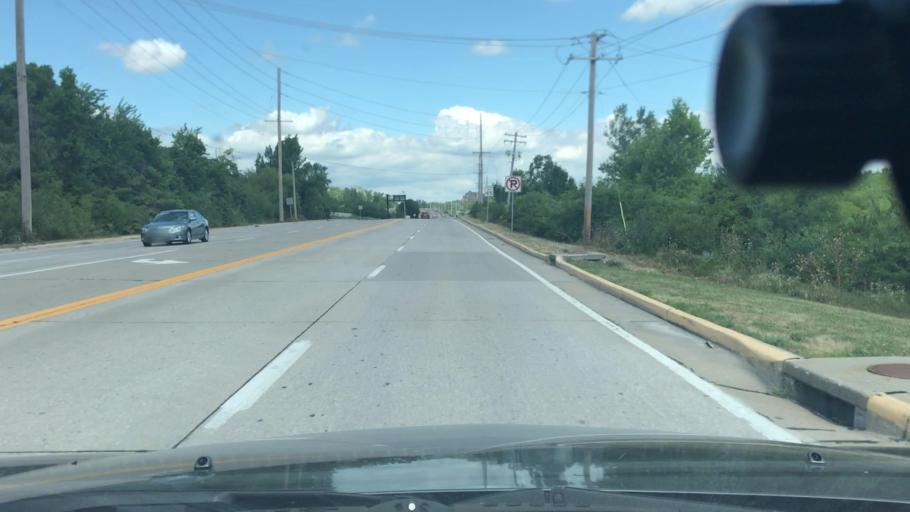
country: US
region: Missouri
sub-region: Saint Charles County
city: Saint Charles
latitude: 38.7493
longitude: -90.5088
